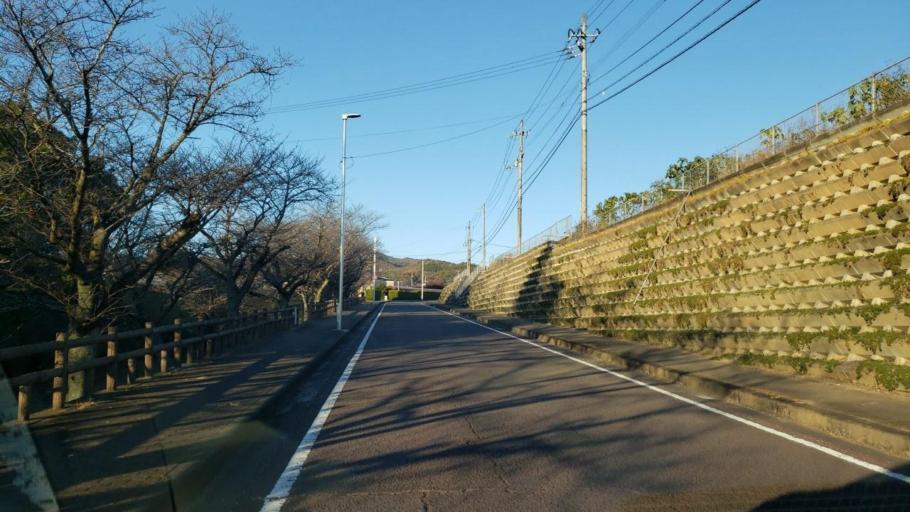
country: JP
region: Tokushima
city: Kamojimacho-jogejima
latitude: 34.0929
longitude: 134.2846
